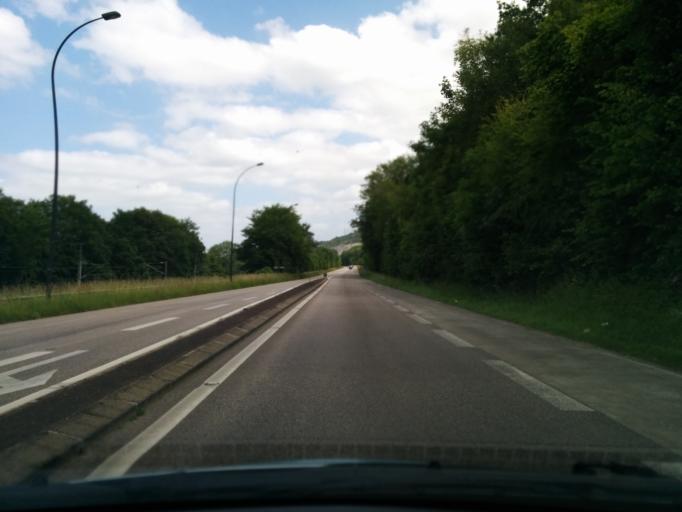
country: FR
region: Ile-de-France
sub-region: Departement des Yvelines
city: Limay
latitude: 48.9701
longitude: 1.7415
